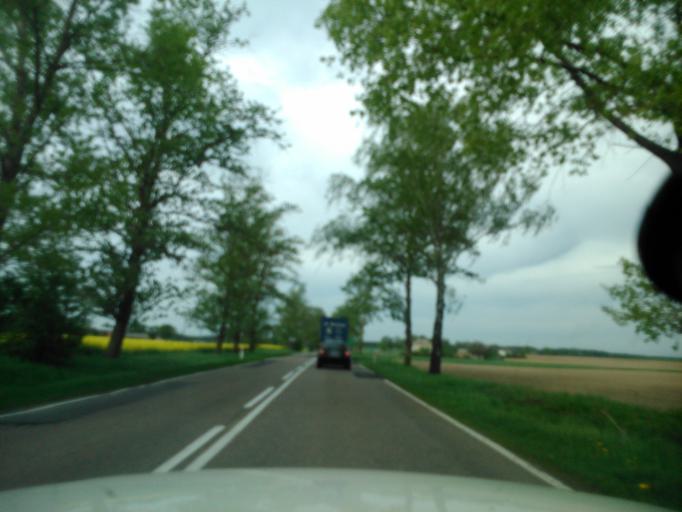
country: PL
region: Kujawsko-Pomorskie
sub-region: Powiat brodnicki
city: Bobrowo
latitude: 53.2226
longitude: 19.1988
